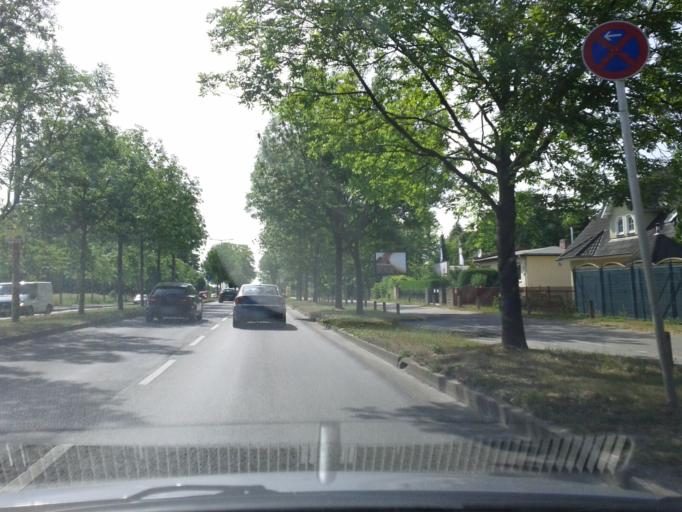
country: DE
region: Berlin
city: Kaulsdorf
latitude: 52.5050
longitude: 13.5956
